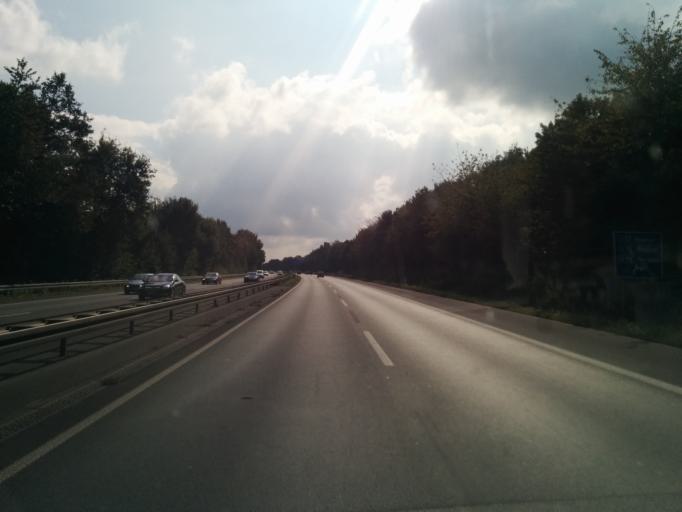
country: DE
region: North Rhine-Westphalia
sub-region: Regierungsbezirk Munster
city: Recklinghausen
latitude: 51.6340
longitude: 7.1680
